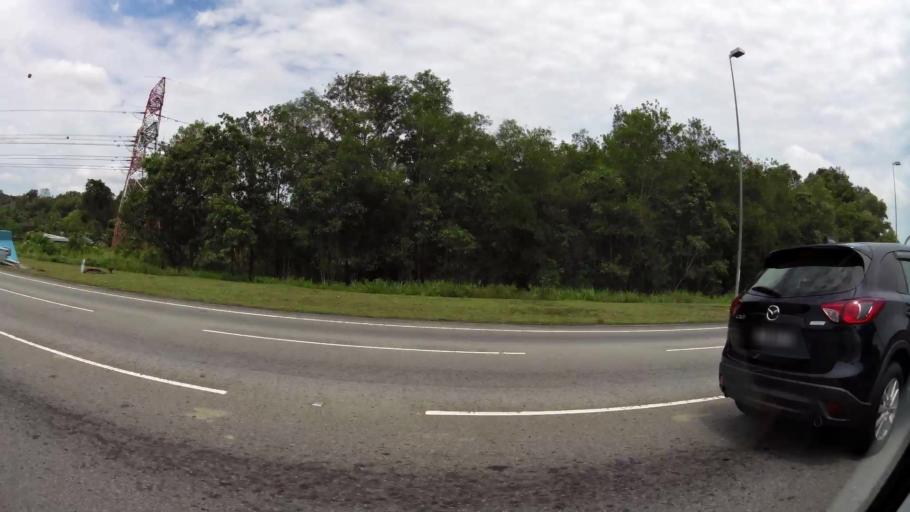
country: BN
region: Brunei and Muara
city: Bandar Seri Begawan
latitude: 4.9138
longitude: 114.9054
